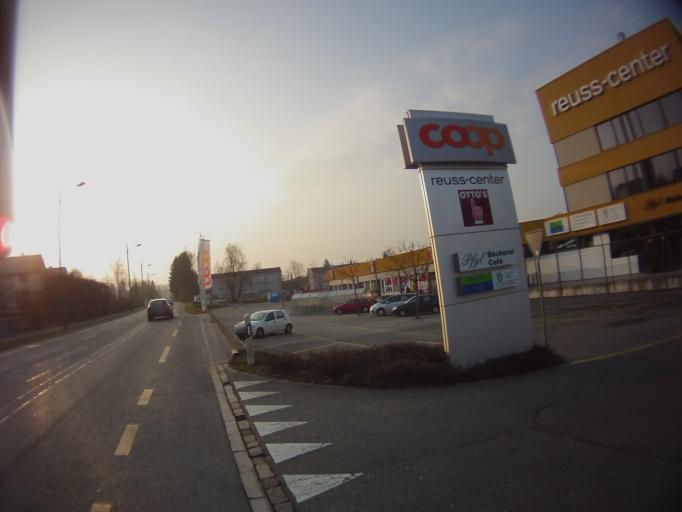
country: CH
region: Zurich
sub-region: Bezirk Affoltern
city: Obfelden
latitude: 47.2674
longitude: 8.4240
